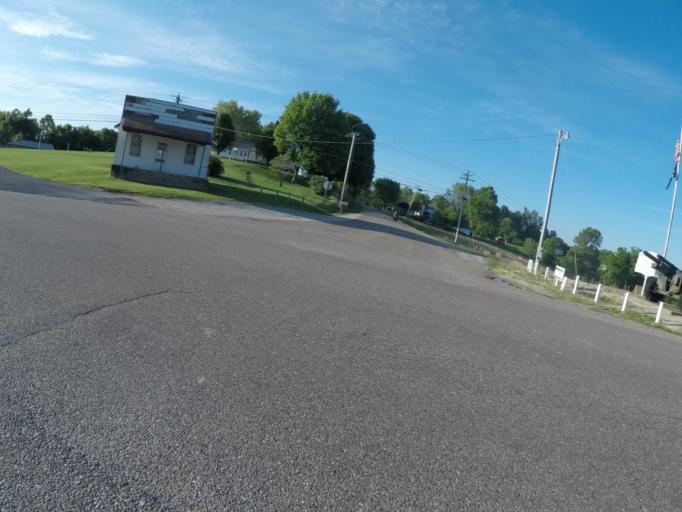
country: US
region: West Virginia
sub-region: Cabell County
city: Huntington
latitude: 38.5536
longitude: -82.4265
